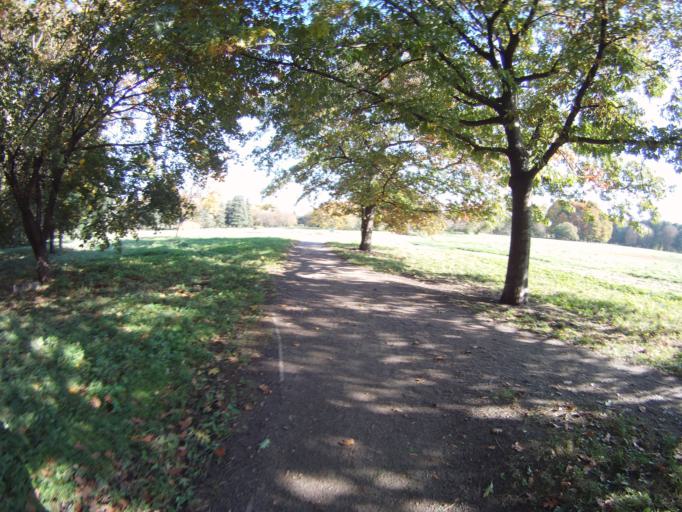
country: BY
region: Minsk
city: Minsk
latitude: 53.9365
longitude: 27.5686
